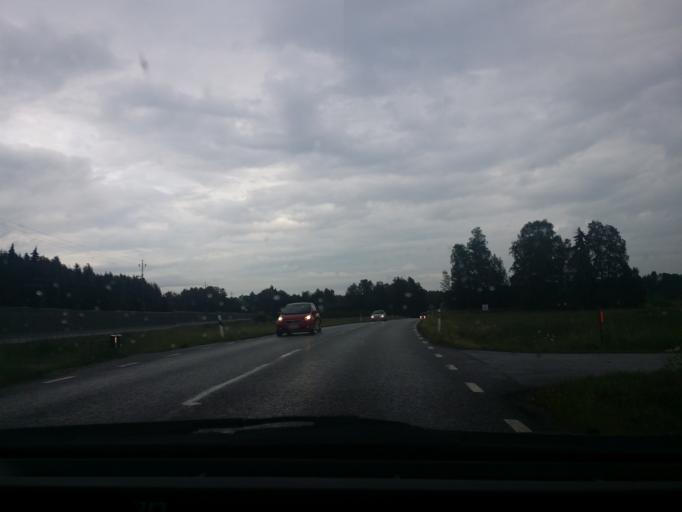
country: SE
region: OErebro
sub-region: Lindesbergs Kommun
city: Frovi
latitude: 59.4665
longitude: 15.3316
